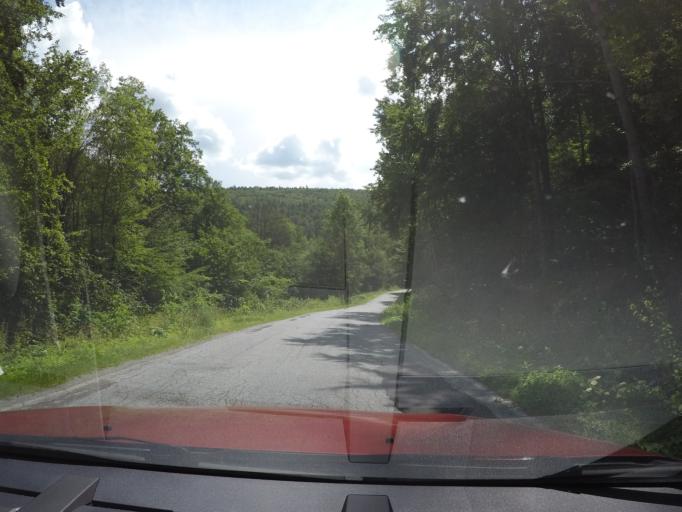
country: SK
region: Kosicky
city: Gelnica
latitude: 48.9231
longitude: 21.0394
